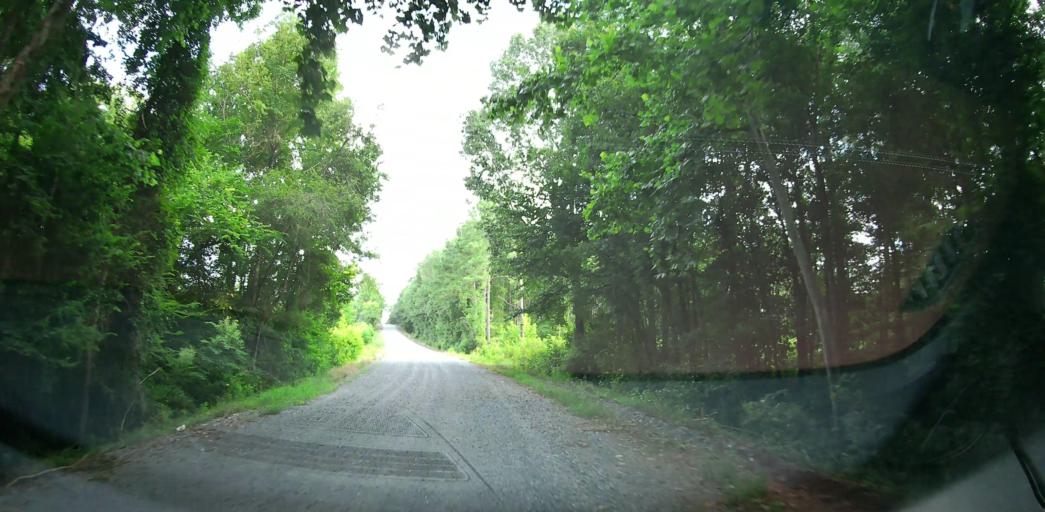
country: US
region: Georgia
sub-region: Bleckley County
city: Cochran
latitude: 32.4260
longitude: -83.4543
